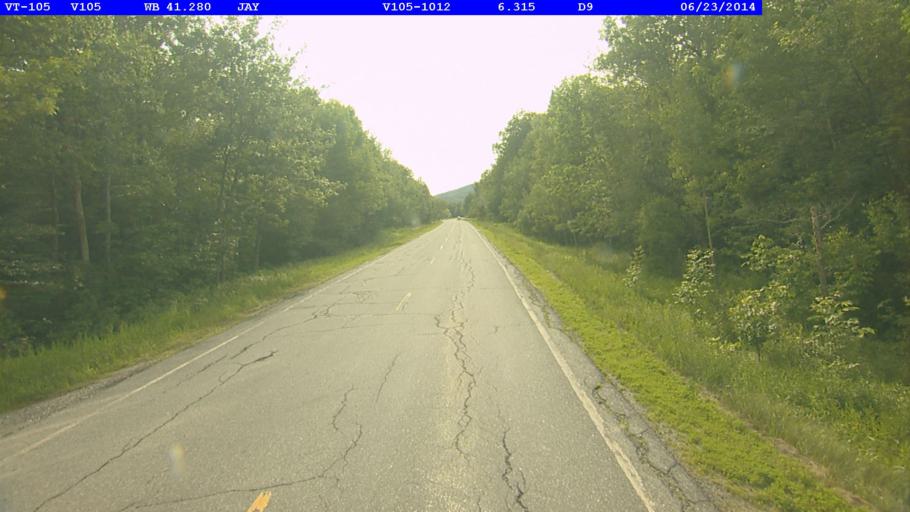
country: CA
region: Quebec
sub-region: Monteregie
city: Sutton
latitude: 44.9728
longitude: -72.4614
